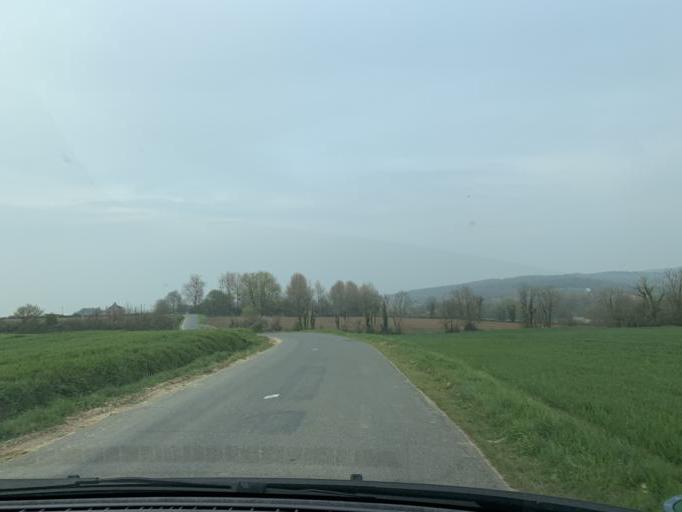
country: FR
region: Nord-Pas-de-Calais
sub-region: Departement du Pas-de-Calais
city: Longfosse
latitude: 50.6891
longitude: 1.7684
